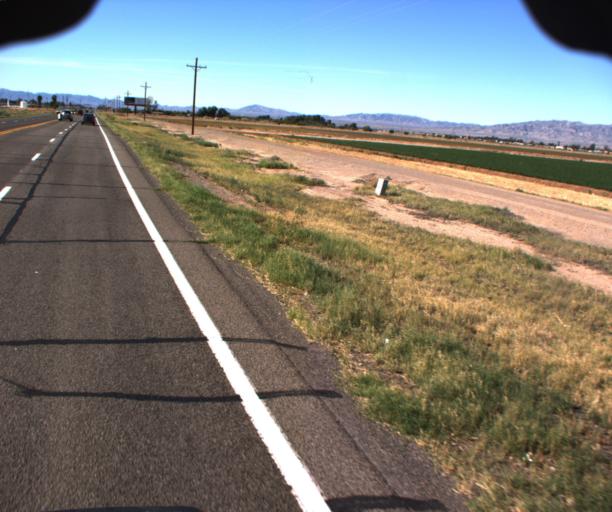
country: US
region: Arizona
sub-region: Mohave County
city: Mohave Valley
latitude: 34.9303
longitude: -114.5979
